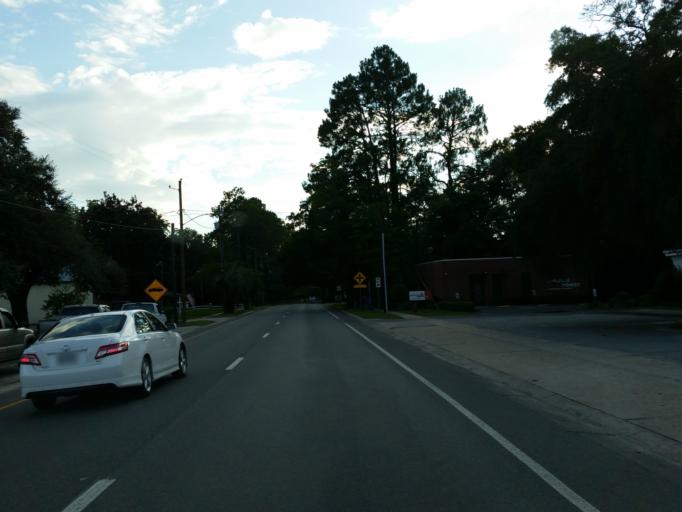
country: US
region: Georgia
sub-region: Clinch County
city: Homerville
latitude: 31.0366
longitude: -82.7484
